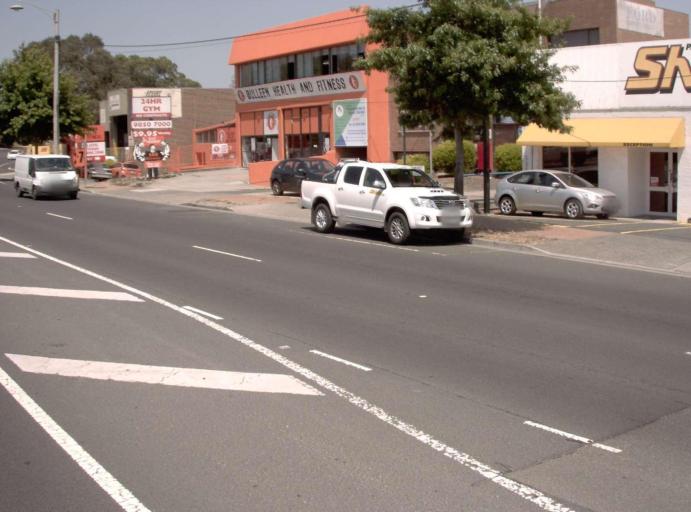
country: AU
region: Victoria
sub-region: Manningham
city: Bulleen
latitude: -37.7642
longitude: 145.0829
